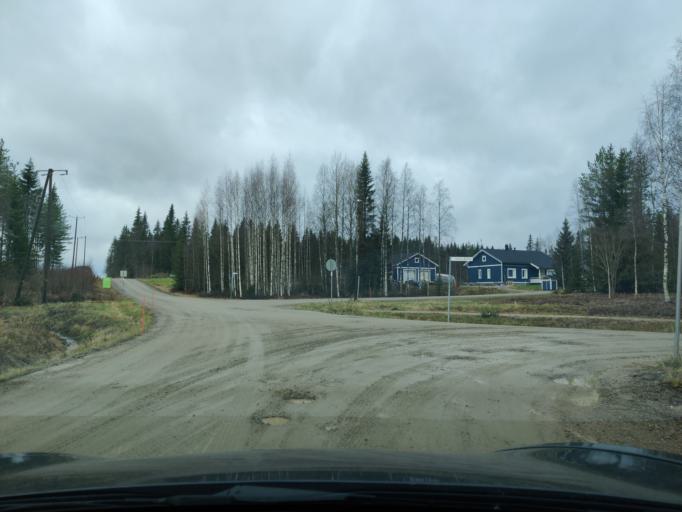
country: FI
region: Northern Savo
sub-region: Ylae-Savo
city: Kiuruvesi
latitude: 63.6392
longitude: 26.6419
